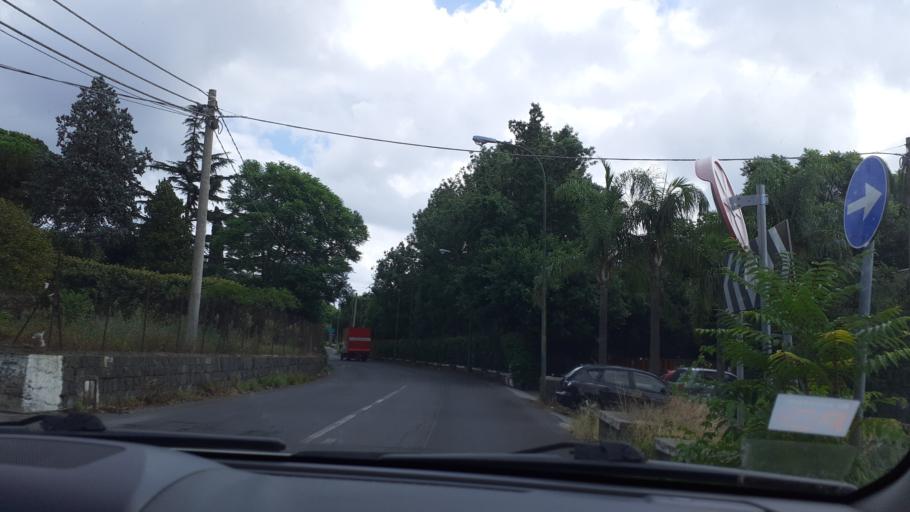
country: IT
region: Sicily
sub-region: Catania
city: Carrubazza-Motta
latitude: 37.5524
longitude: 15.1060
